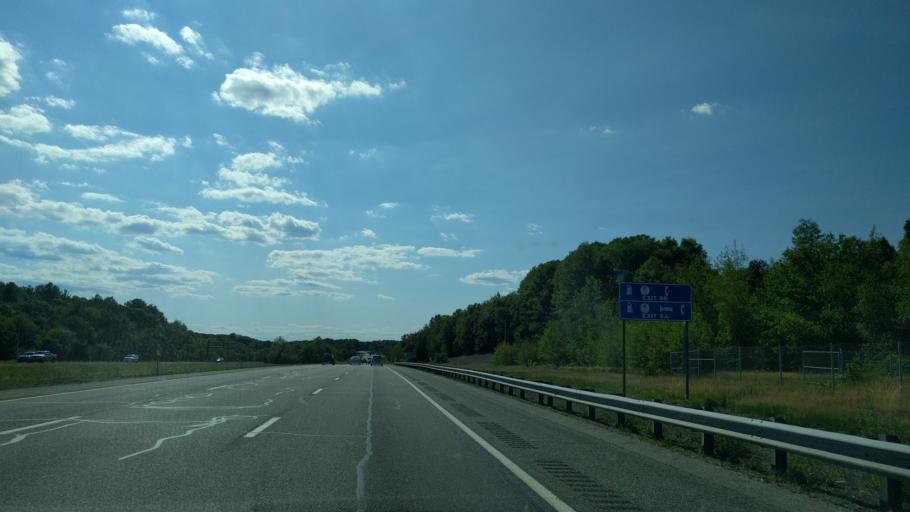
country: US
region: Rhode Island
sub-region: Providence County
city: Cumberland Hill
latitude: 41.9420
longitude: -71.4638
